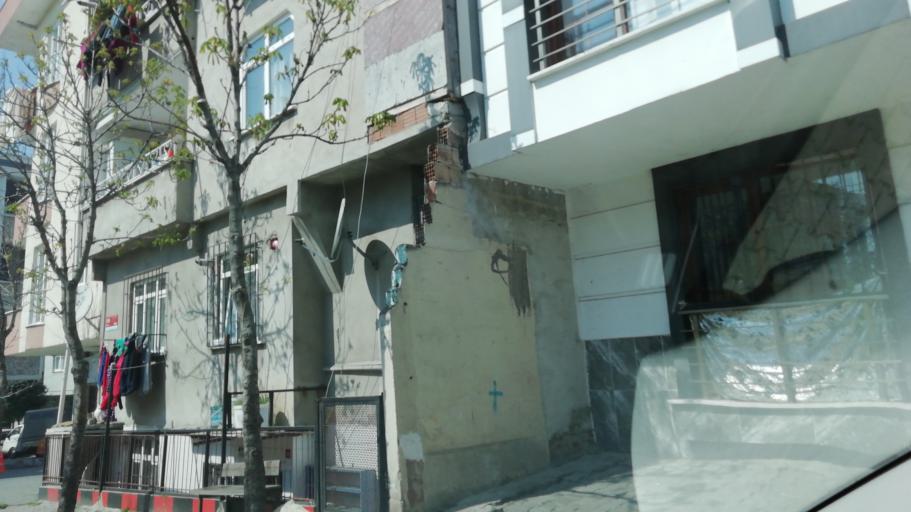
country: TR
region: Istanbul
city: Mahmutbey
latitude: 41.0398
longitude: 28.8224
